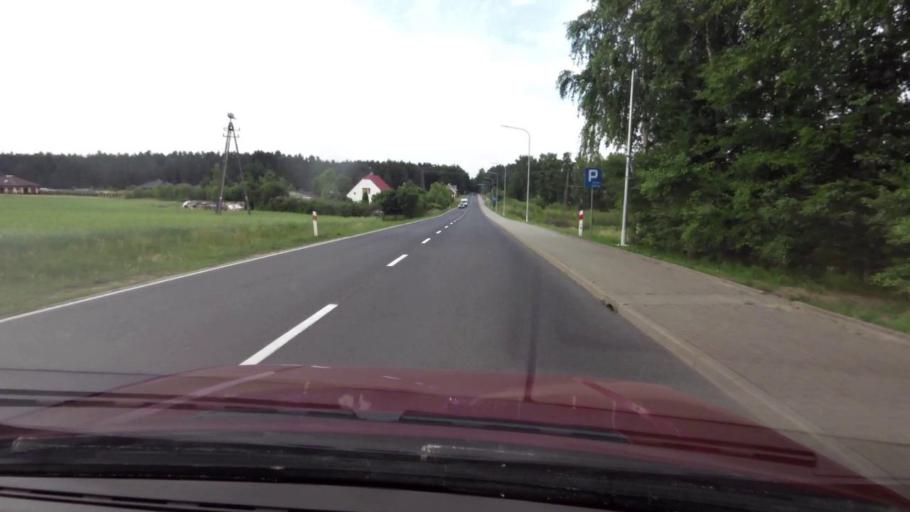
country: PL
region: Pomeranian Voivodeship
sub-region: Powiat bytowski
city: Trzebielino
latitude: 54.2479
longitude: 17.1000
